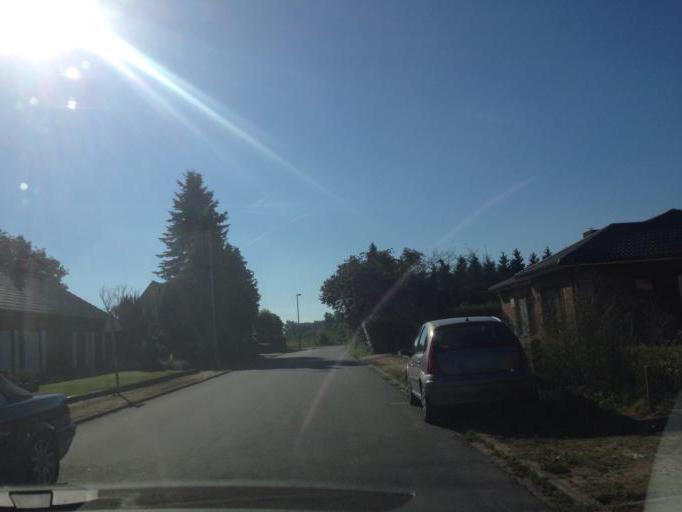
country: BE
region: Flanders
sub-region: Provincie Antwerpen
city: Geel
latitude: 51.1645
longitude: 5.0139
